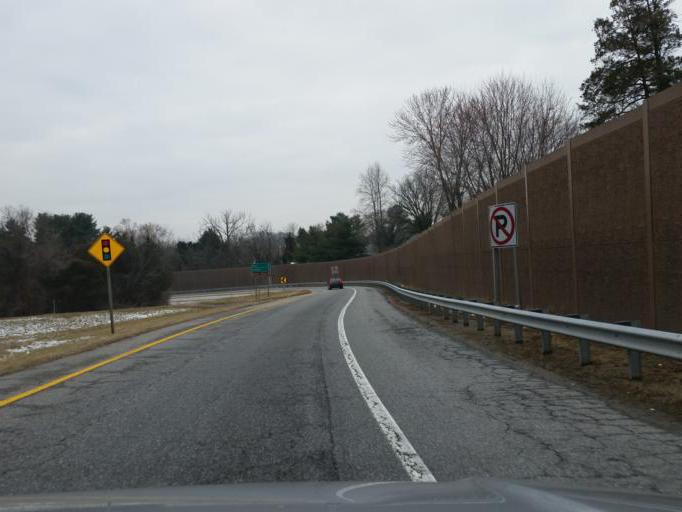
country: US
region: Maryland
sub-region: Howard County
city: Elkridge
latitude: 39.2224
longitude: -76.7031
